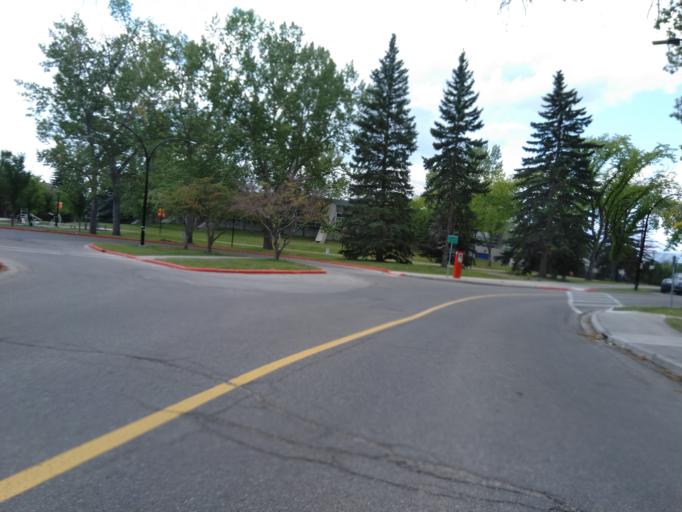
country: CA
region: Alberta
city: Calgary
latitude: 51.0764
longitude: -114.1335
